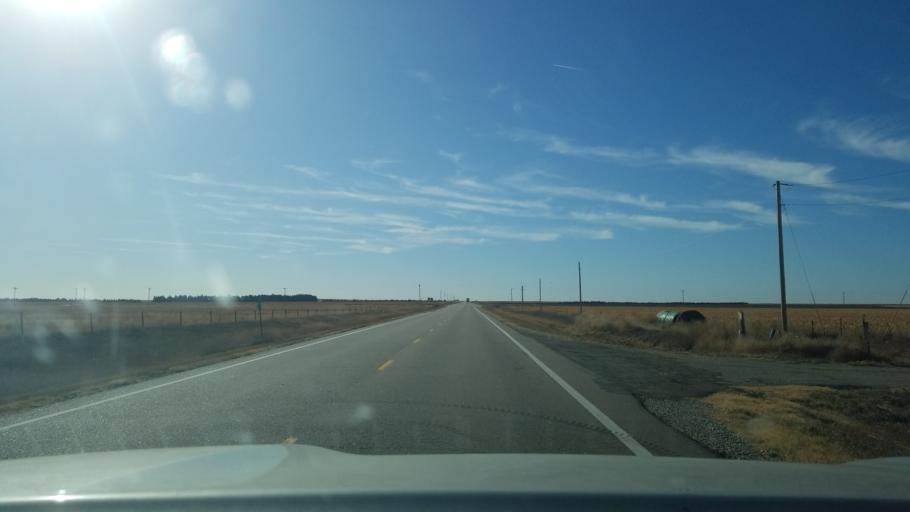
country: US
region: Kansas
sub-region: Ness County
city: Ness City
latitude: 38.3663
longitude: -99.8981
